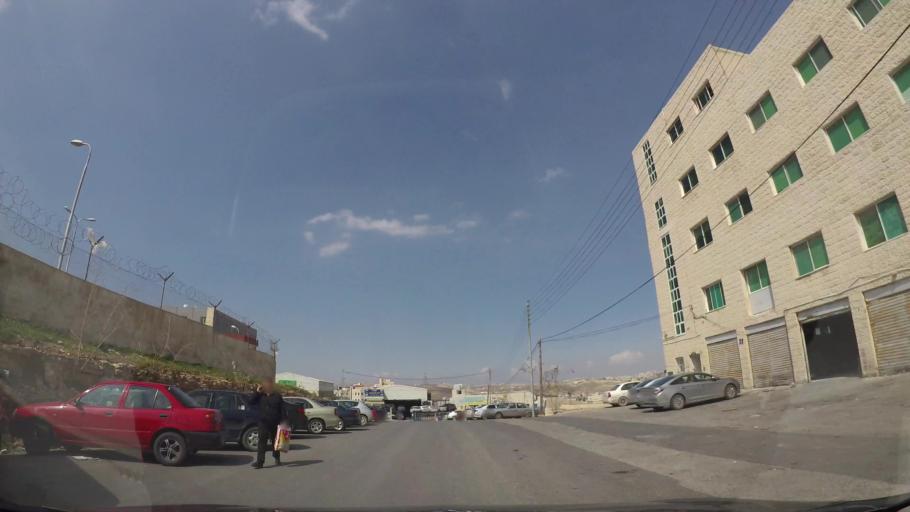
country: JO
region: Zarqa
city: Russeifa
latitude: 31.9969
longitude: 35.9977
